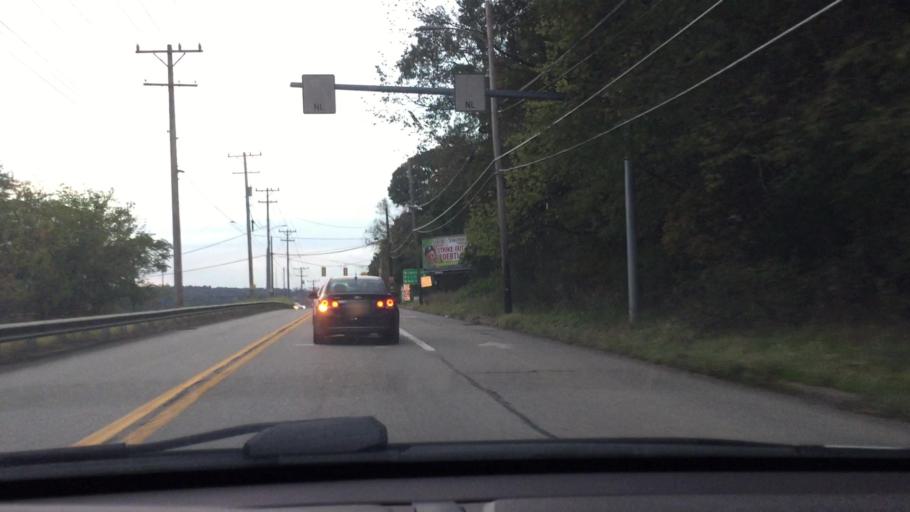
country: US
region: Pennsylvania
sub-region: Westmoreland County
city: New Kensington
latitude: 40.5648
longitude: -79.7749
